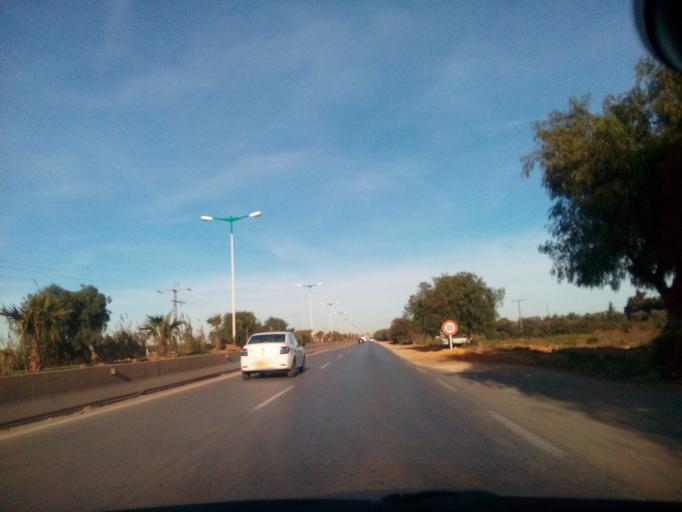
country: DZ
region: Mostaganem
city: Mostaganem
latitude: 35.8590
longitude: 0.1613
